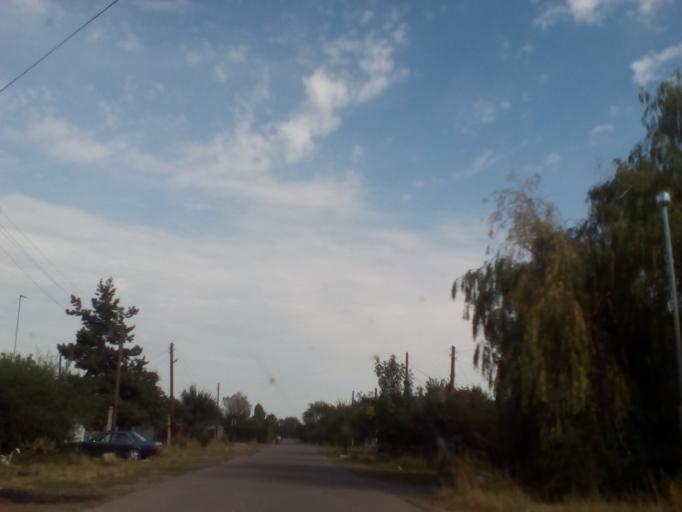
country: KZ
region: Almaty Oblysy
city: Burunday
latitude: 43.1657
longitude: 76.4054
